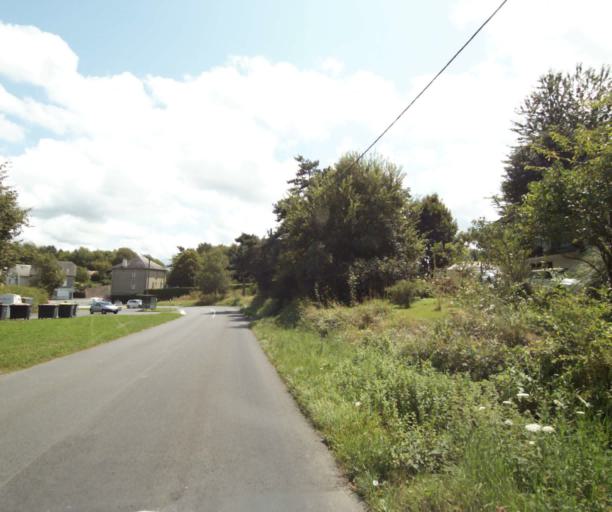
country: FR
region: Limousin
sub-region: Departement de la Correze
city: Sainte-Fortunade
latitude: 45.2016
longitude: 1.8296
